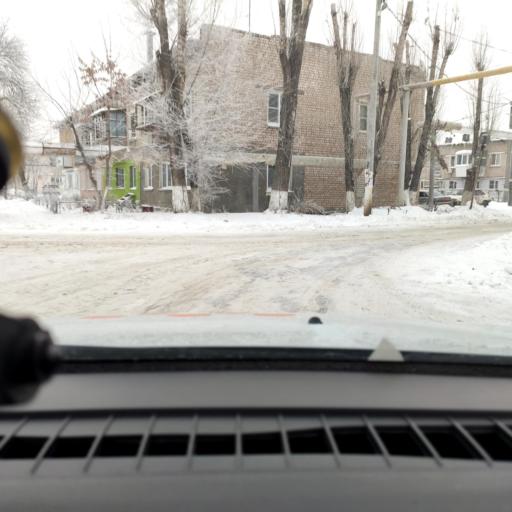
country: RU
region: Samara
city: Dubovyy Umet
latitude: 53.0788
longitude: 50.2299
